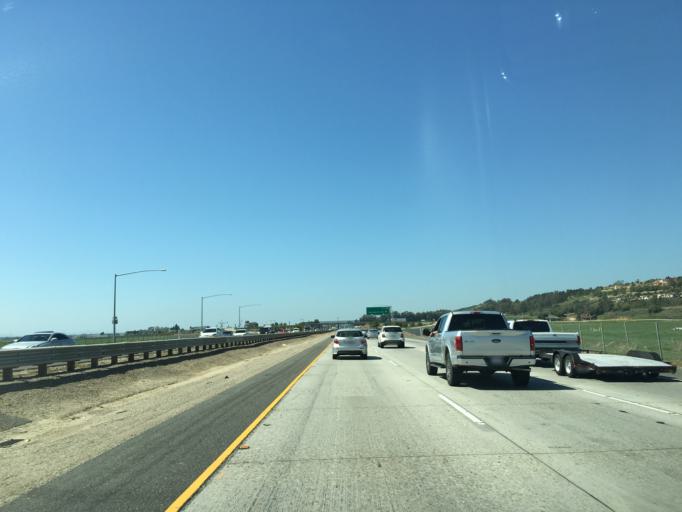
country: US
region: California
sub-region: Ventura County
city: Camarillo
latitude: 34.2199
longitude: -119.0784
